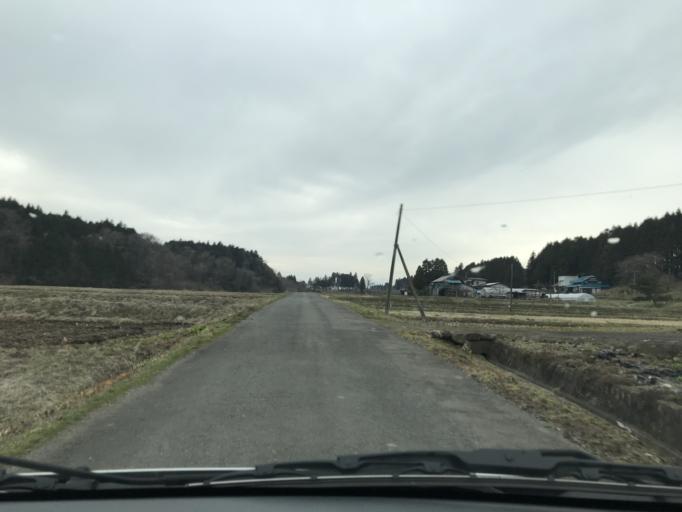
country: JP
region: Iwate
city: Mizusawa
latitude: 39.0941
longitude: 141.1076
